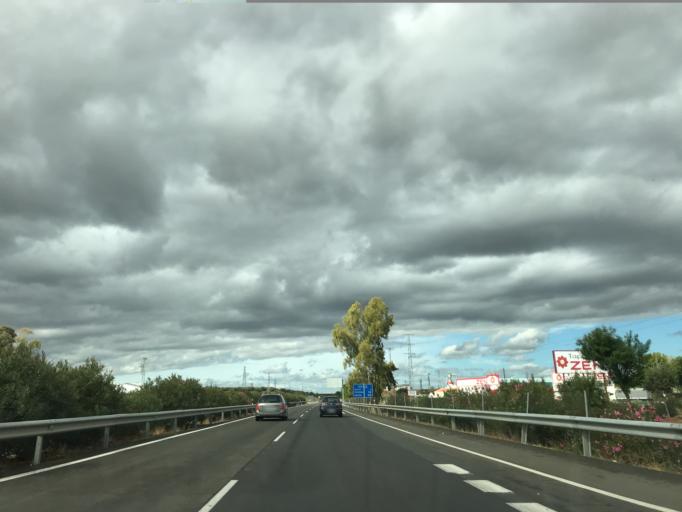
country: ES
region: Andalusia
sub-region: Province of Cordoba
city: Villa del Rio
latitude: 37.9868
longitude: -4.3063
